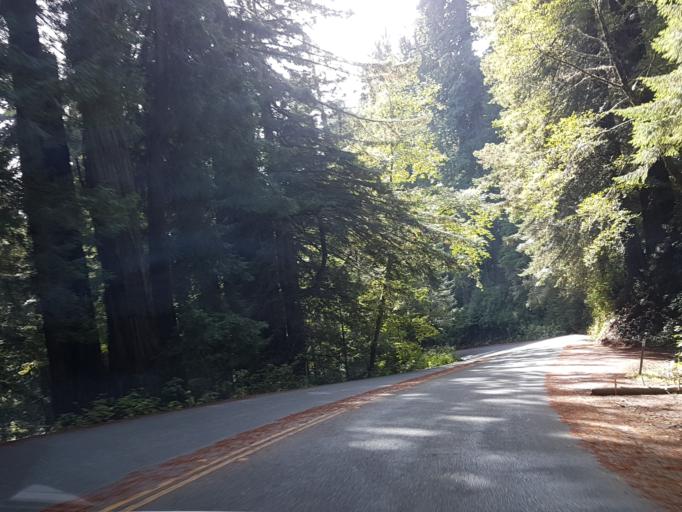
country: US
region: California
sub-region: Del Norte County
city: Bertsch-Oceanview
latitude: 41.4484
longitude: -124.0389
